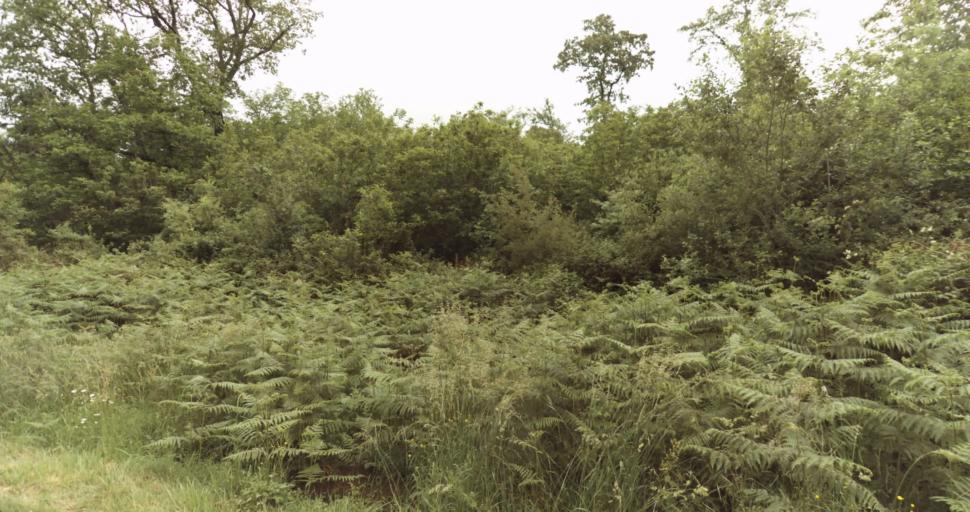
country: FR
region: Aquitaine
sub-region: Departement de la Dordogne
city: Belves
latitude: 44.7163
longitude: 0.9424
